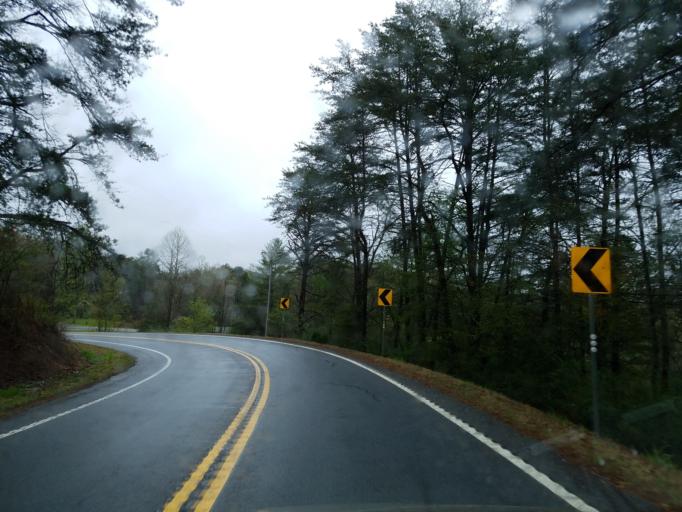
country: US
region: Georgia
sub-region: Fannin County
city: Blue Ridge
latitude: 34.8679
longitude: -84.2342
